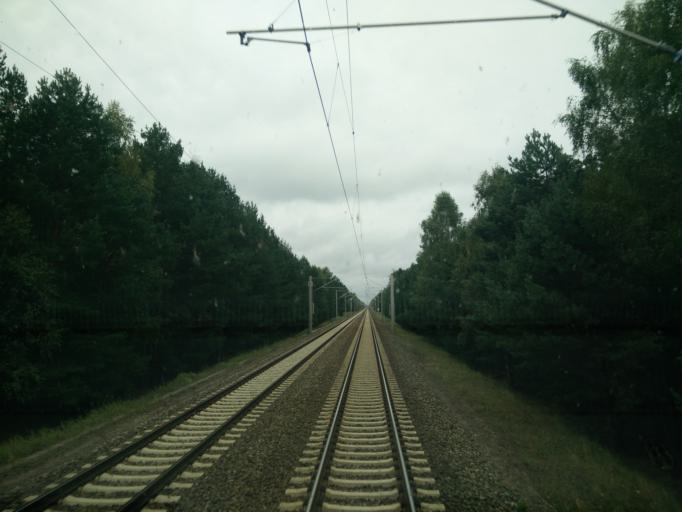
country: DE
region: Brandenburg
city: Kasel-Golzig
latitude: 52.0067
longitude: 13.7533
